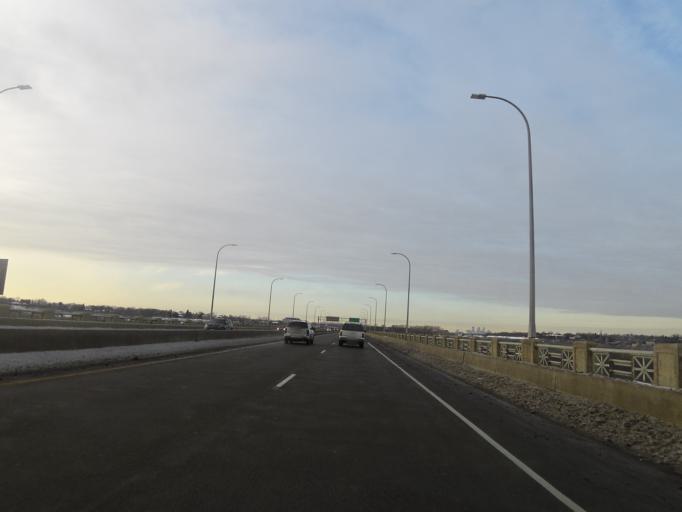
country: US
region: Minnesota
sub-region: Dakota County
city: Mendota Heights
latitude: 44.8848
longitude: -93.1730
